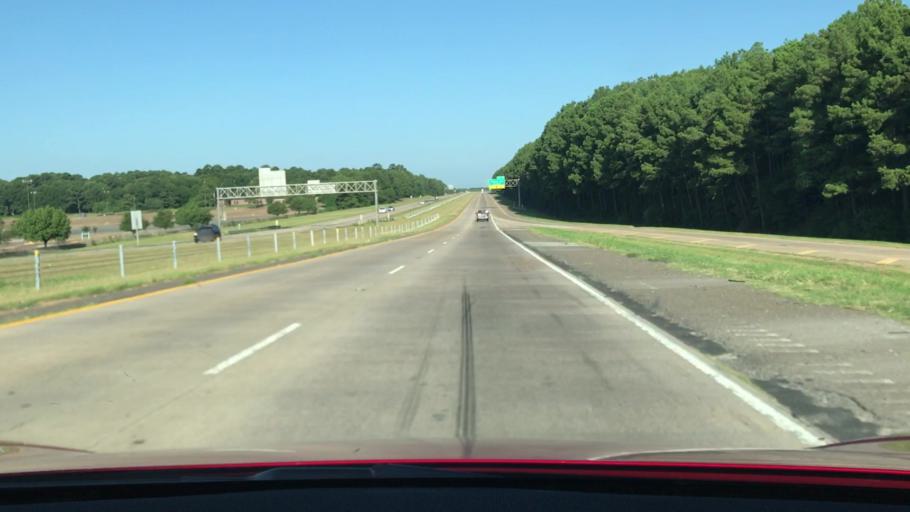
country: US
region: Louisiana
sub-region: Caddo Parish
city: Shreveport
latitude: 32.4174
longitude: -93.7998
